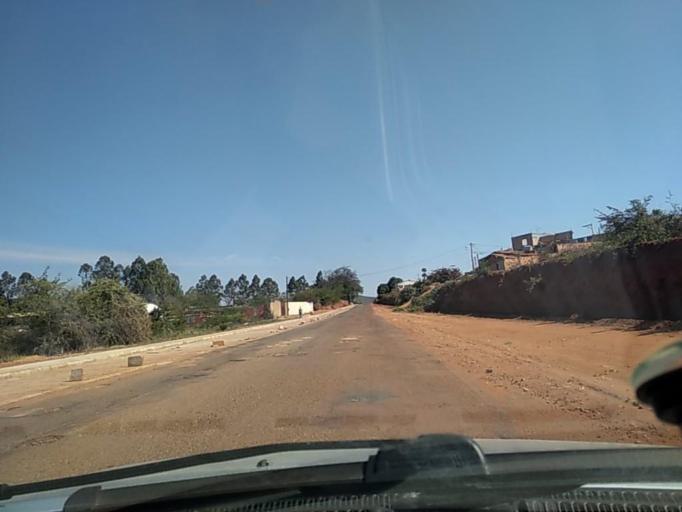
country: BR
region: Bahia
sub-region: Caetite
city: Caetite
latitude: -14.0497
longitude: -42.4850
